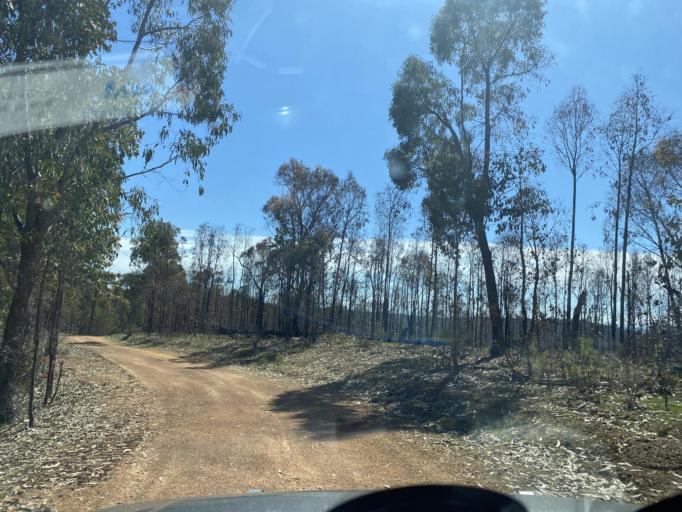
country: AU
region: Victoria
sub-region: Benalla
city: Benalla
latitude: -36.7397
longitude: 146.1797
